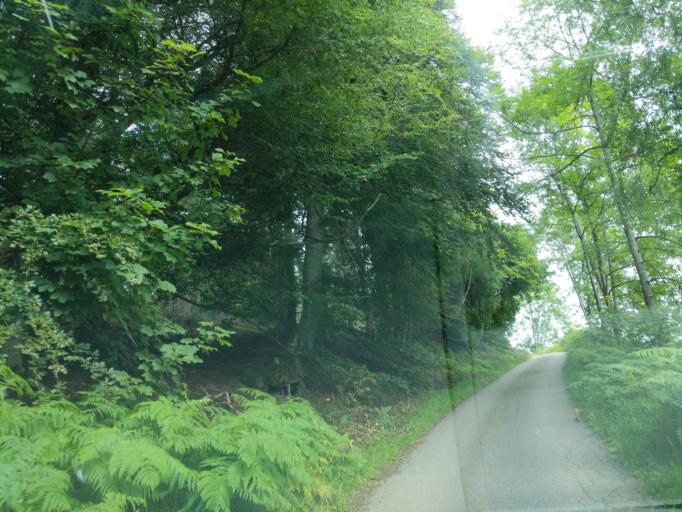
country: GB
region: Scotland
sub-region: Moray
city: Rothes
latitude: 57.4699
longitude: -3.2362
